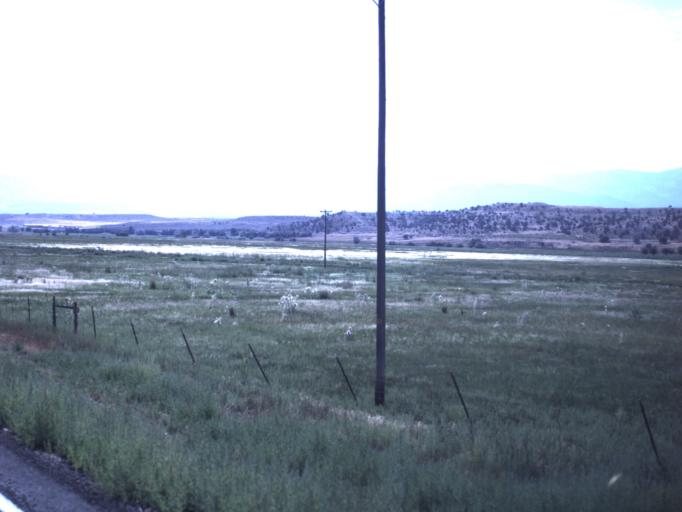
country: US
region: Utah
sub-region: Sanpete County
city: Moroni
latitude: 39.5249
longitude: -111.5626
